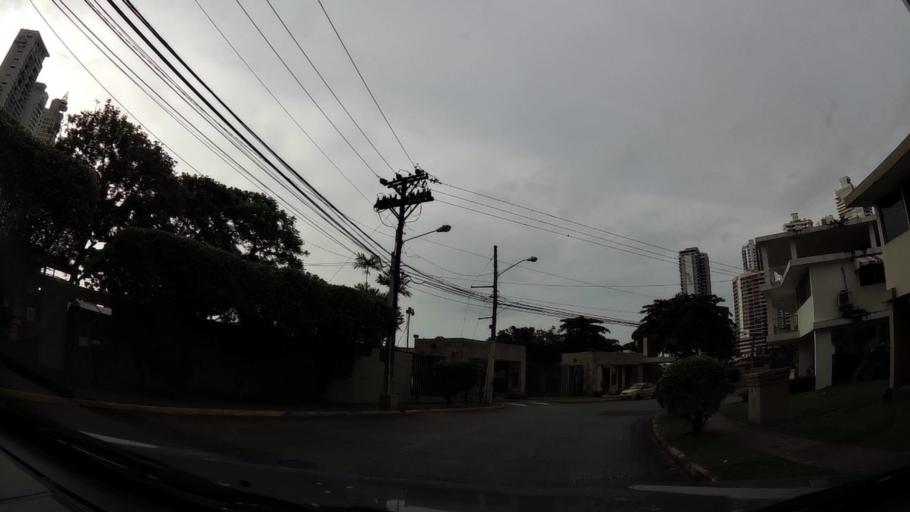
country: PA
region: Panama
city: Panama
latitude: 8.9762
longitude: -79.5105
